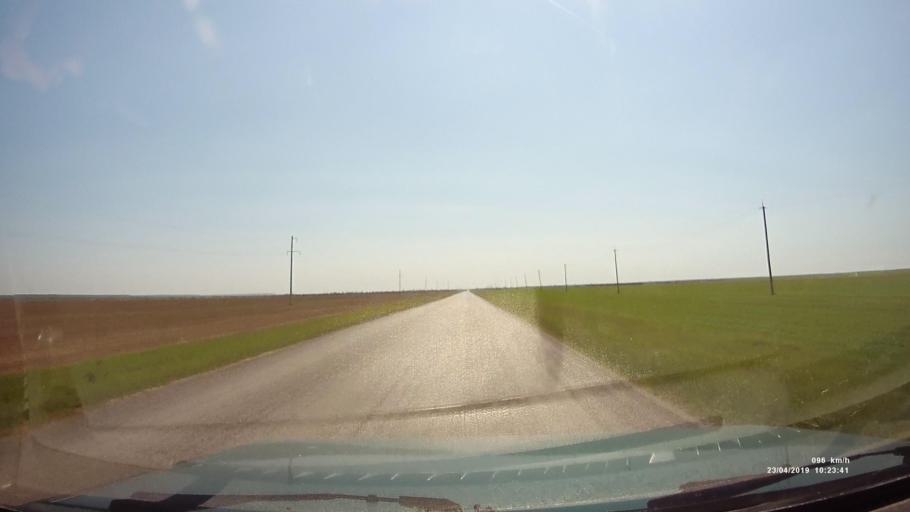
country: RU
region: Rostov
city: Sovetskoye
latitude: 46.6454
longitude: 42.4287
